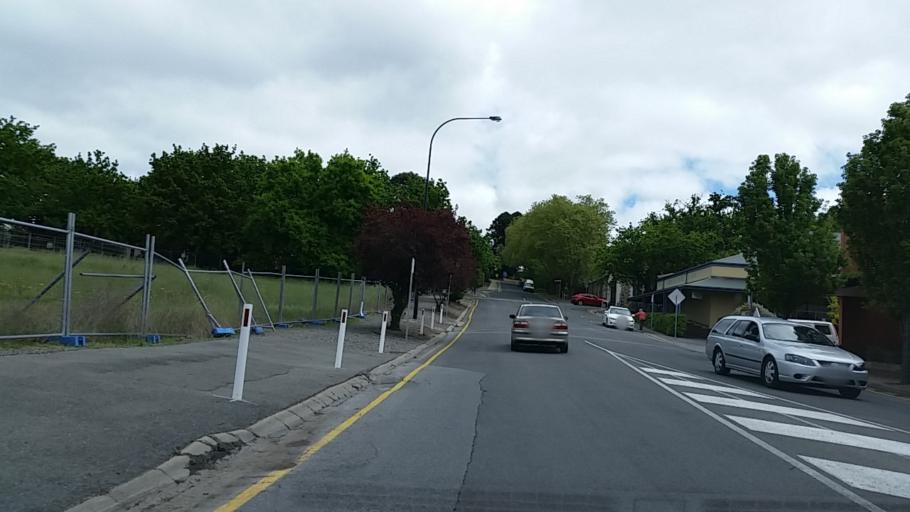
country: AU
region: South Australia
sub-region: Mount Barker
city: Mount Barker
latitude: -35.0648
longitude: 138.8586
